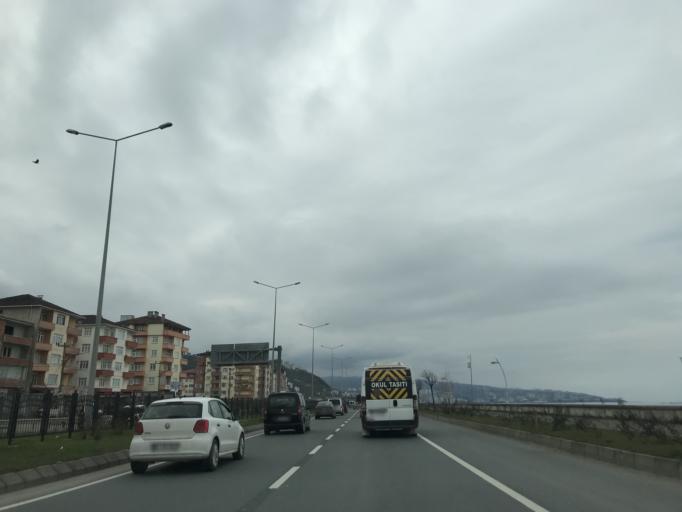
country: TR
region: Trabzon
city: Arsin
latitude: 40.9546
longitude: 39.9225
